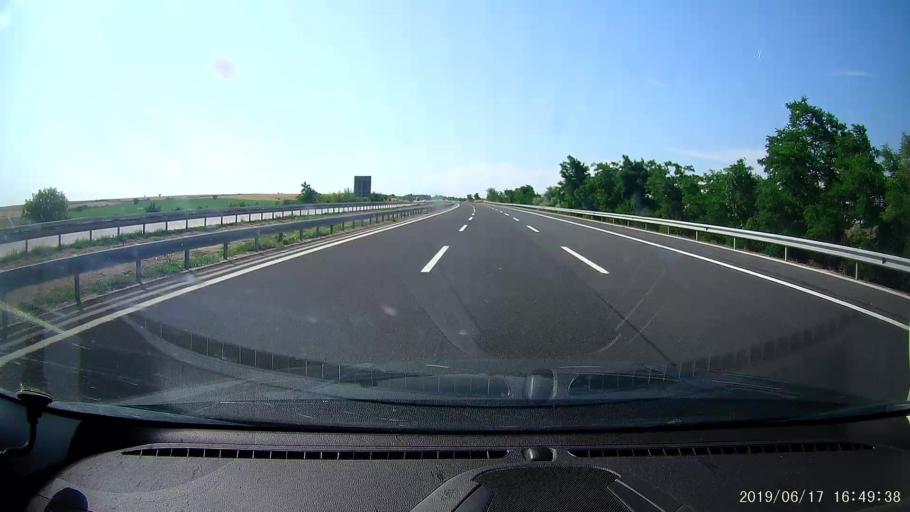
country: TR
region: Kirklareli
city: Babaeski
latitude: 41.5121
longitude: 27.1091
